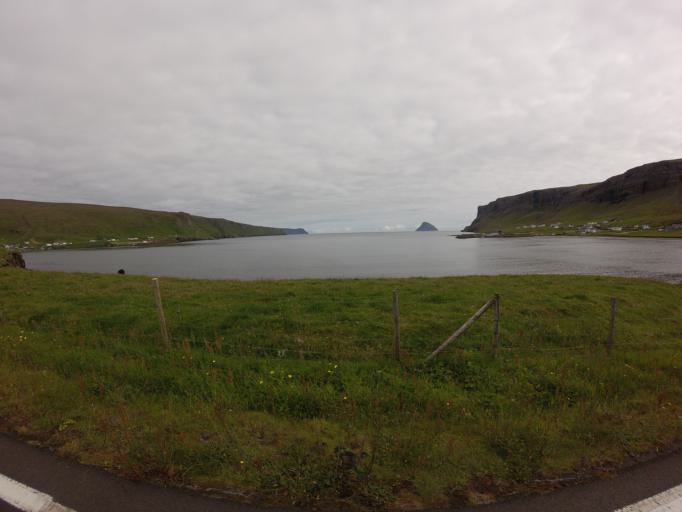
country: FO
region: Suduroy
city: Tvoroyri
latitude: 61.5936
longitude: -6.9441
